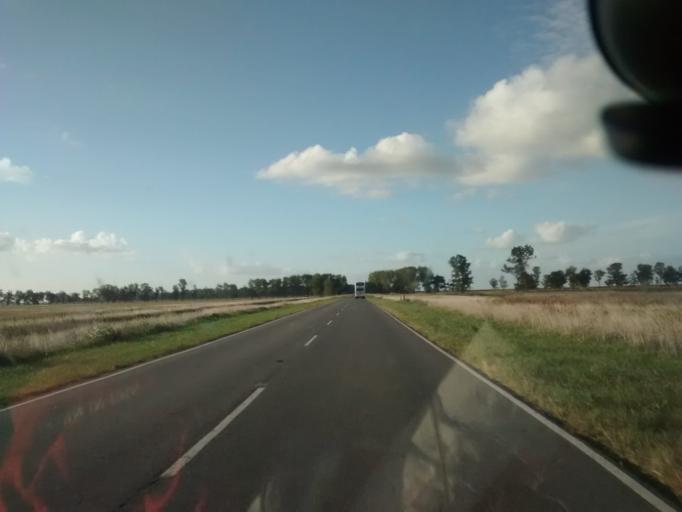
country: AR
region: Buenos Aires
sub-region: Partido de General Belgrano
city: General Belgrano
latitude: -36.1605
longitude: -58.5947
